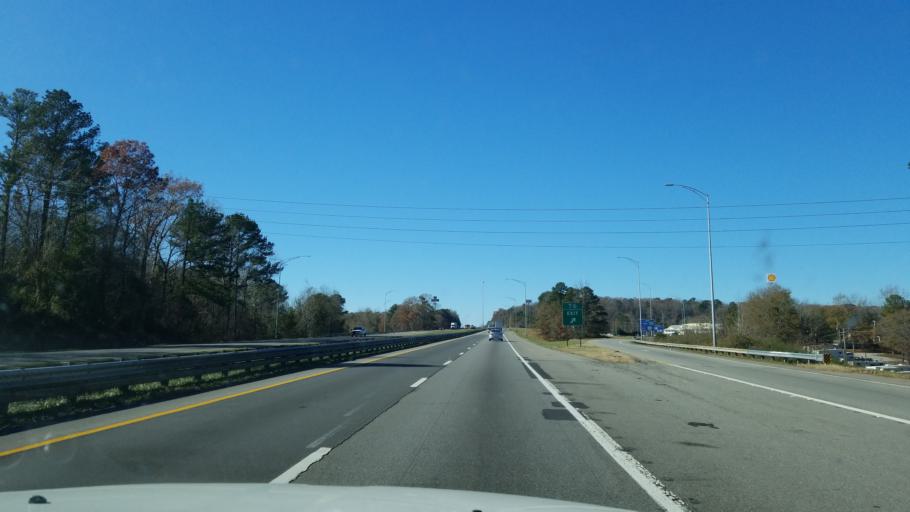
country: US
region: Alabama
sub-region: Tuscaloosa County
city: Holt
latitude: 33.1732
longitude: -87.4689
